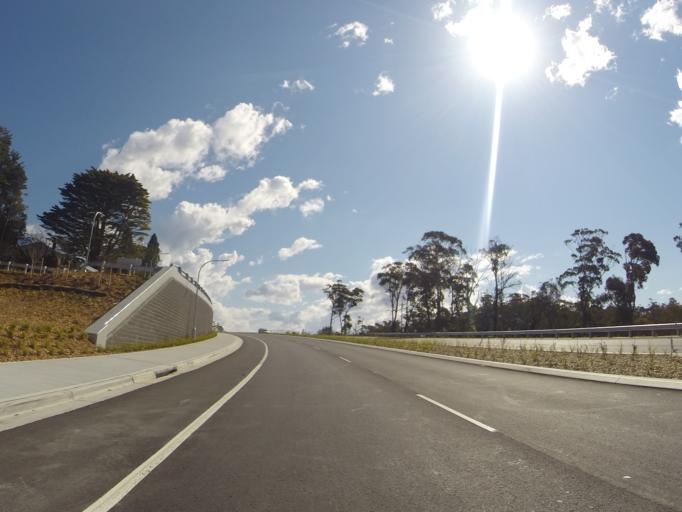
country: AU
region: New South Wales
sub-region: Blue Mountains Municipality
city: Lawson
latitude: -33.7236
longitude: 150.4193
